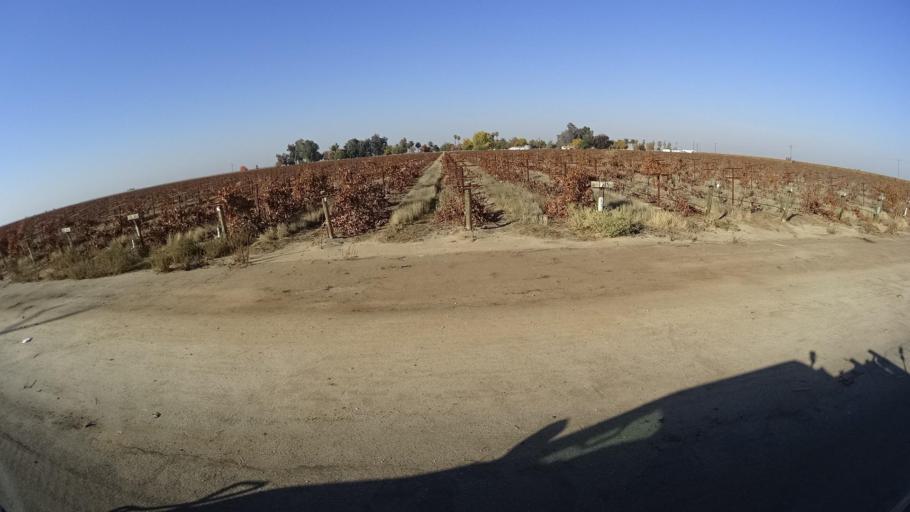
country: US
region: California
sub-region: Tulare County
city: Richgrove
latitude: 35.7454
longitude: -119.1695
